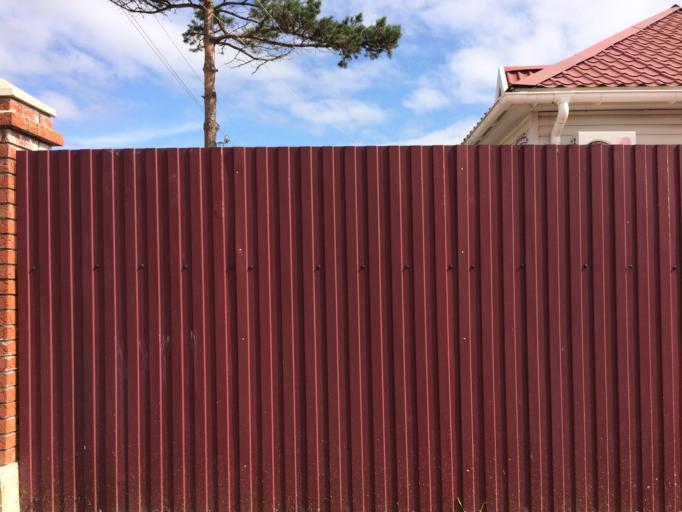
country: RU
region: Primorskiy
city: Dal'nerechensk
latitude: 45.9279
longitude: 133.7245
